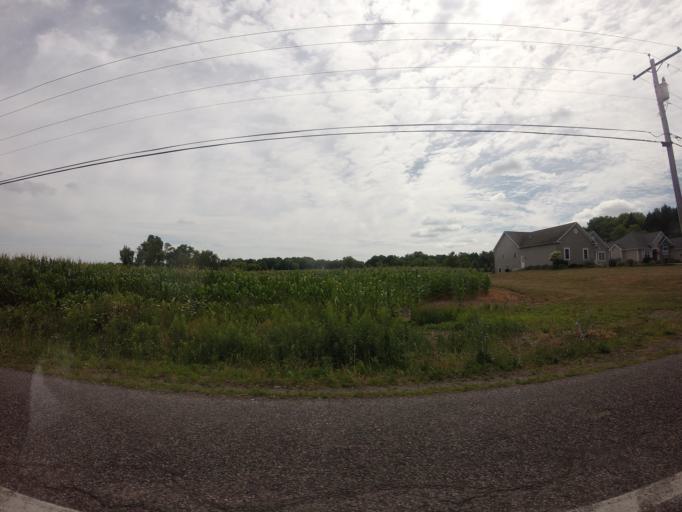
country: US
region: New York
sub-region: Onondaga County
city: Camillus
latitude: 43.0148
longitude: -76.3047
